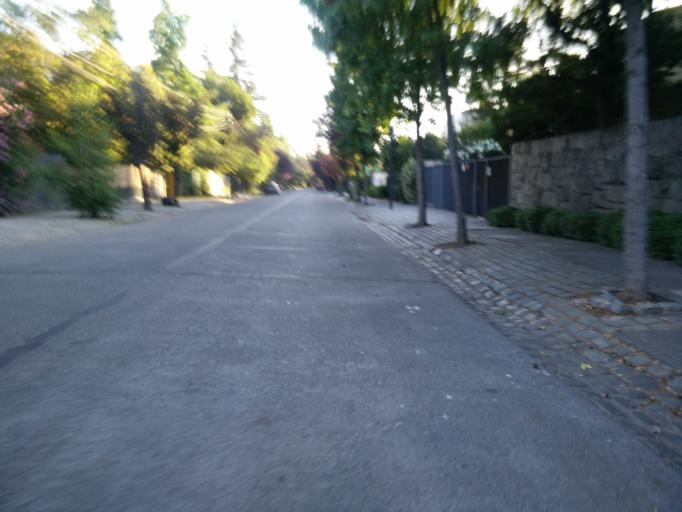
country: CL
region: Santiago Metropolitan
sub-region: Provincia de Santiago
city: Villa Presidente Frei, Nunoa, Santiago, Chile
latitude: -33.3879
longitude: -70.5834
